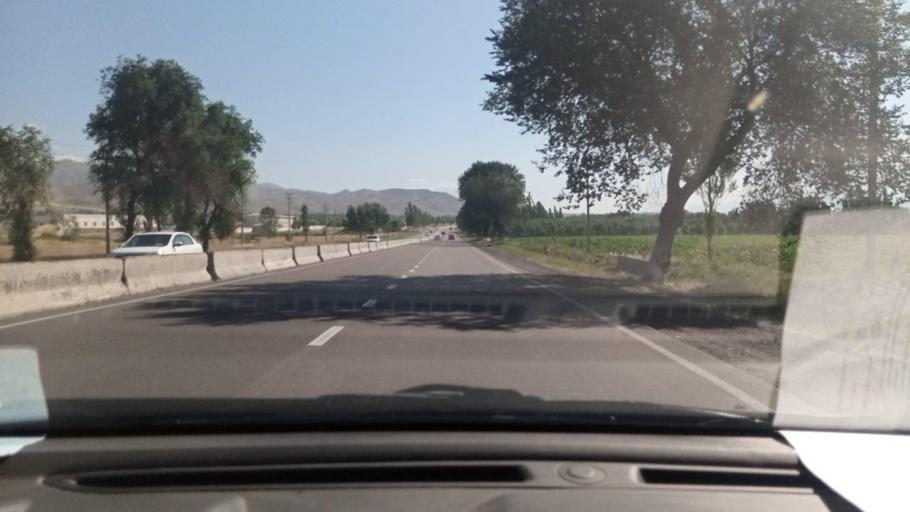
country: UZ
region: Toshkent
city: Ohangaron
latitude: 40.9212
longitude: 69.8384
